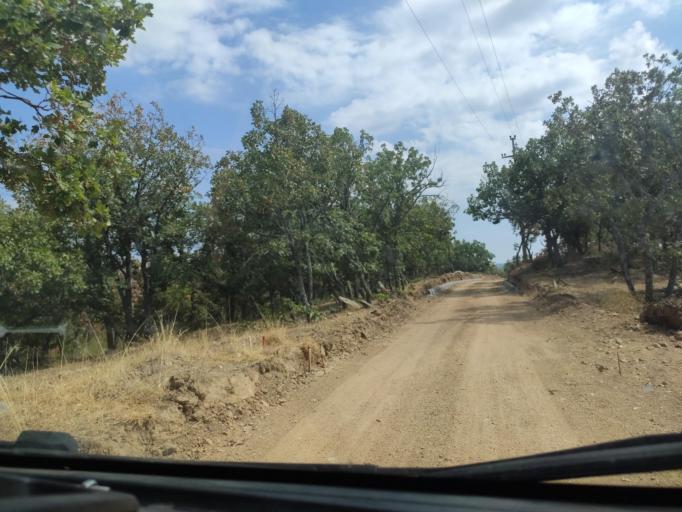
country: MK
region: Radovis
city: Radovish
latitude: 41.6659
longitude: 22.4079
